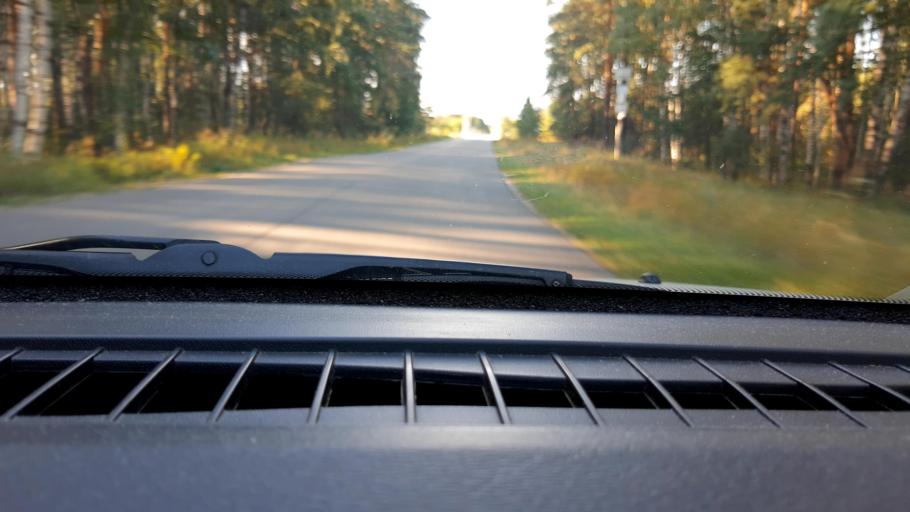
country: RU
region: Nizjnij Novgorod
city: Babino
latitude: 56.3319
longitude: 43.6197
